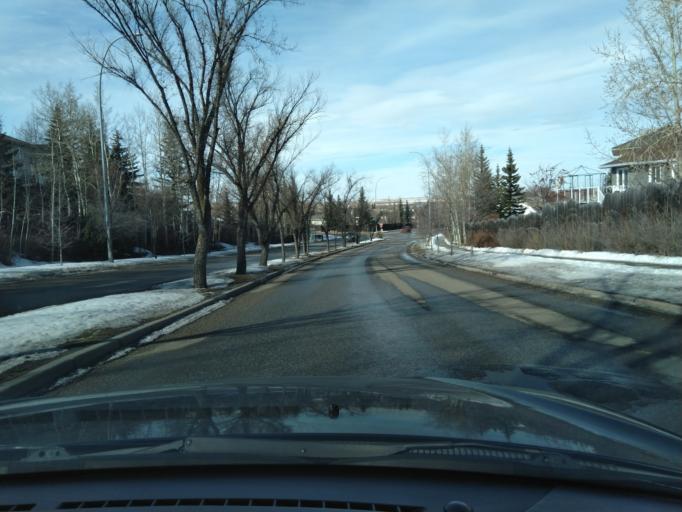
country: CA
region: Alberta
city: Calgary
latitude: 51.1336
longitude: -114.1344
